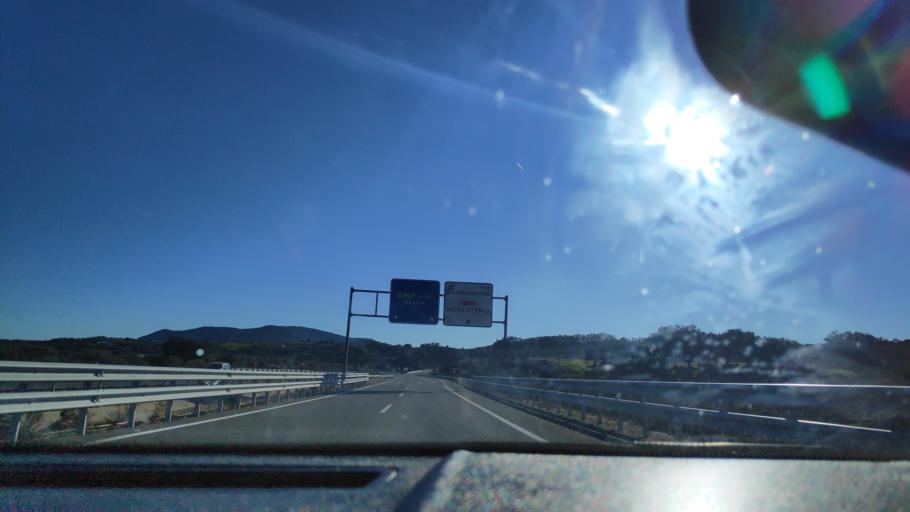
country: ES
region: Extremadura
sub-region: Provincia de Badajoz
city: Monesterio
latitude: 38.1115
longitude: -6.2706
